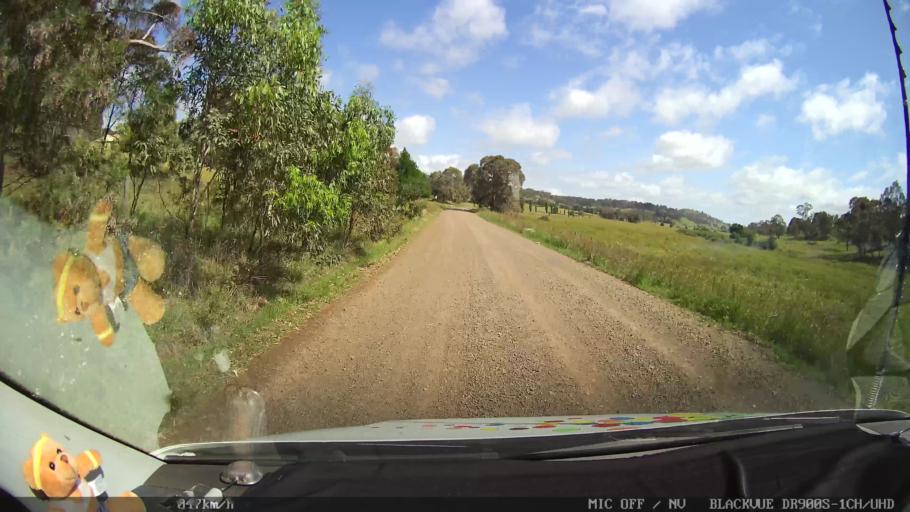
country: AU
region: New South Wales
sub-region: Guyra
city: Guyra
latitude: -29.9751
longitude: 151.6995
